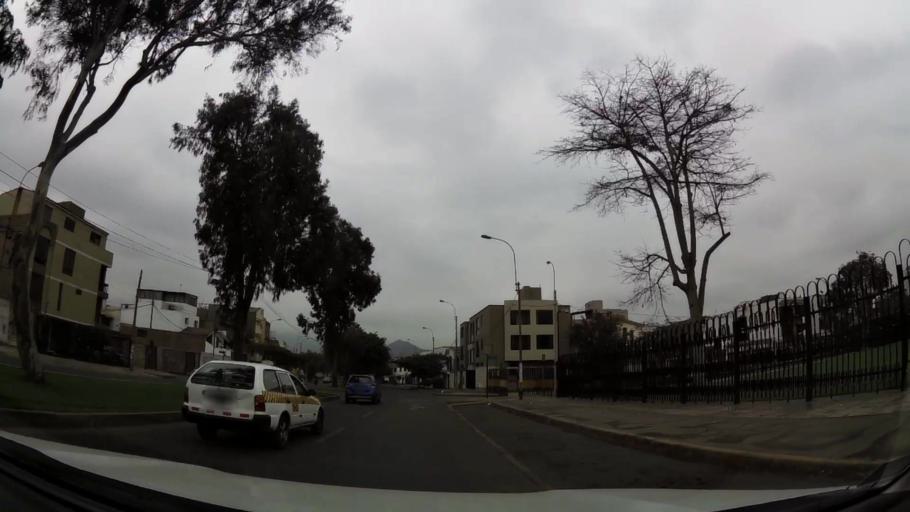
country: PE
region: Lima
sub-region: Lima
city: La Molina
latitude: -12.0707
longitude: -76.9486
